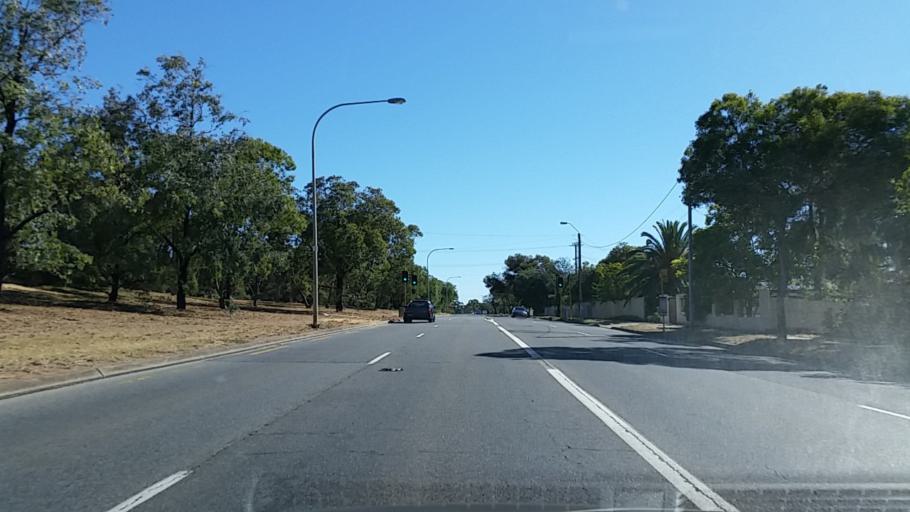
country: AU
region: South Australia
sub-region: Salisbury
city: Ingle Farm
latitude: -34.8318
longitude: 138.6289
